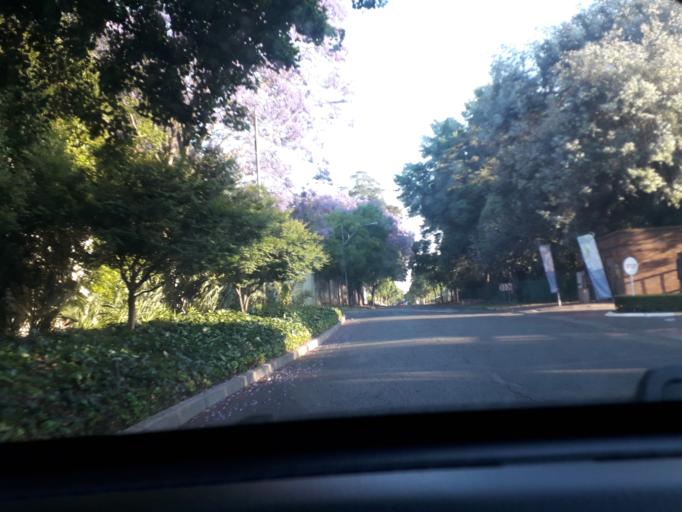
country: ZA
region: Gauteng
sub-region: City of Johannesburg Metropolitan Municipality
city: Johannesburg
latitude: -26.1522
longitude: 28.0537
